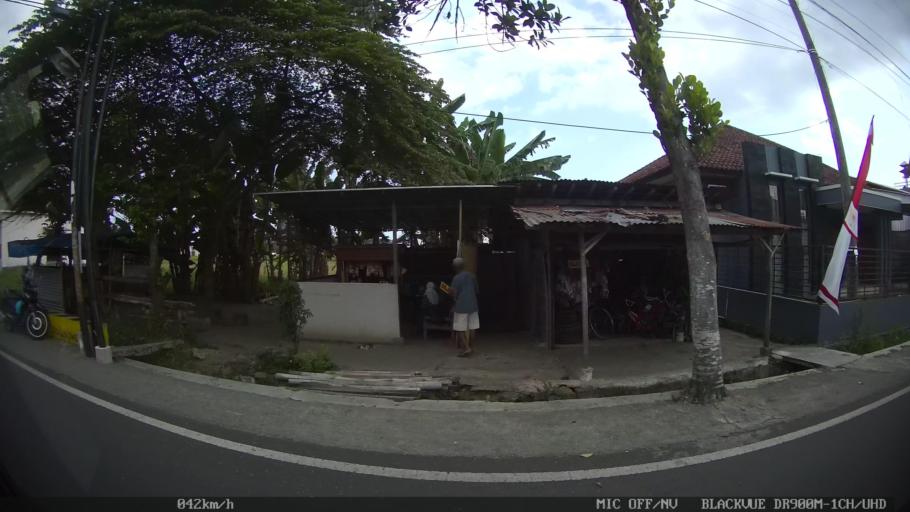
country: ID
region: Daerah Istimewa Yogyakarta
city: Gamping Lor
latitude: -7.7838
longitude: 110.3334
